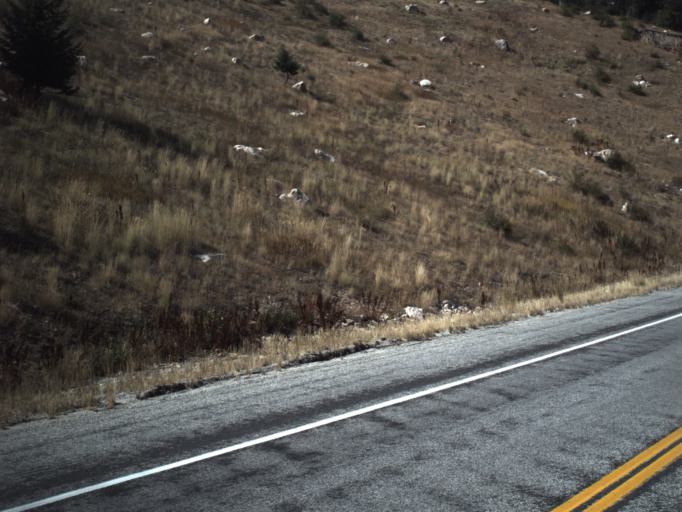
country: US
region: Utah
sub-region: Morgan County
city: Mountain Green
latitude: 41.2141
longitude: -111.8521
